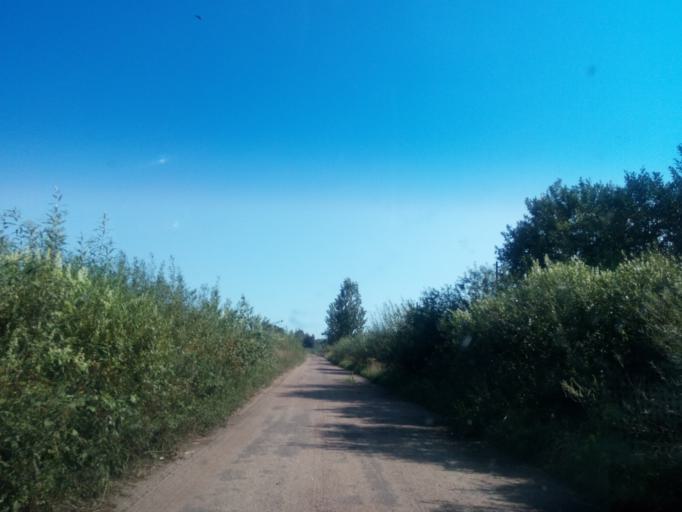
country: BY
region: Vitebsk
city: Dzisna
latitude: 55.6459
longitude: 28.2461
